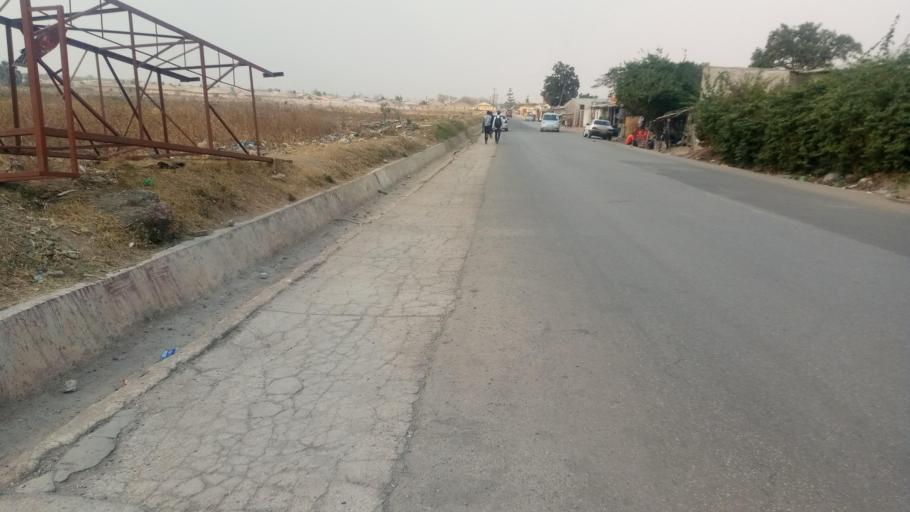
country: ZM
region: Lusaka
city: Lusaka
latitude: -15.4454
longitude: 28.3736
